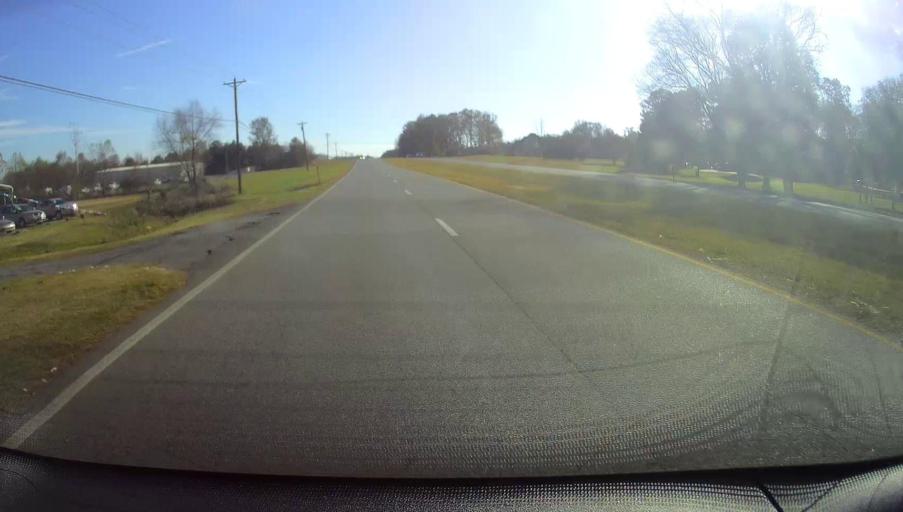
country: US
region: Alabama
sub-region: Limestone County
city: Athens
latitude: 34.7237
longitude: -86.9570
